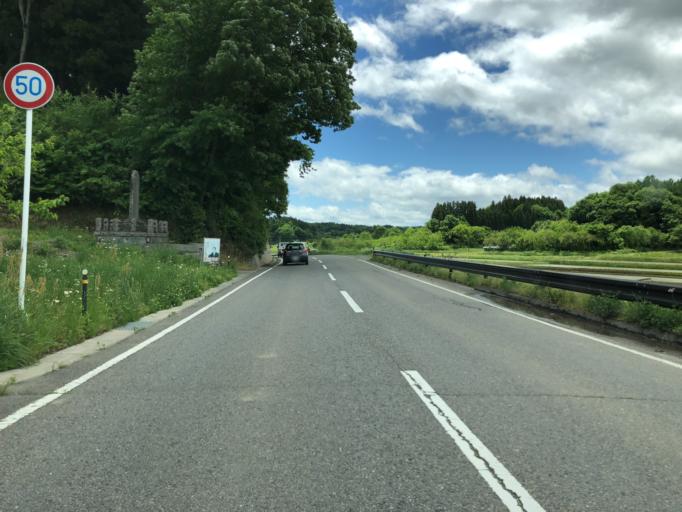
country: JP
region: Fukushima
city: Motomiya
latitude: 37.5172
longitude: 140.4696
